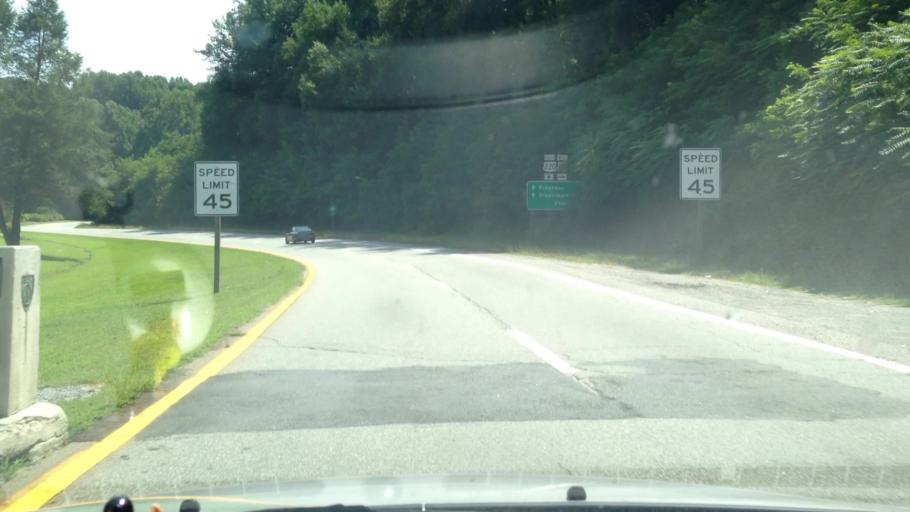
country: US
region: Virginia
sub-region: City of Martinsville
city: Martinsville
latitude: 36.6638
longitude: -79.8830
